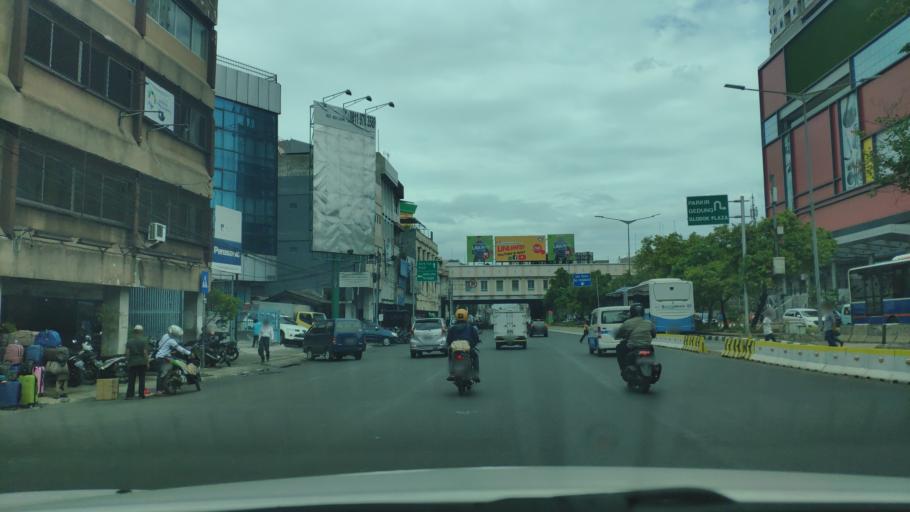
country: ID
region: Jakarta Raya
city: Jakarta
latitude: -6.1443
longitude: 106.8153
